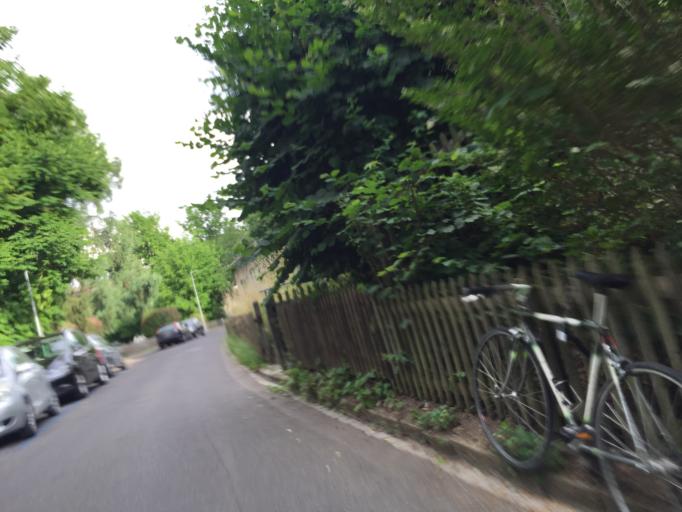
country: CH
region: Bern
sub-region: Bern-Mittelland District
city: Koniz
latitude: 46.9330
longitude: 7.4320
